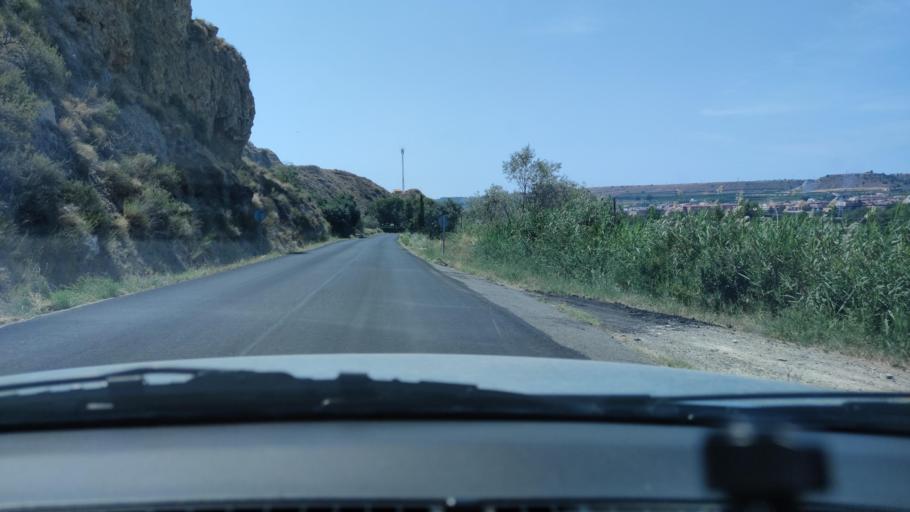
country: ES
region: Catalonia
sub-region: Provincia de Lleida
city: Alfarras
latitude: 41.8354
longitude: 0.5828
